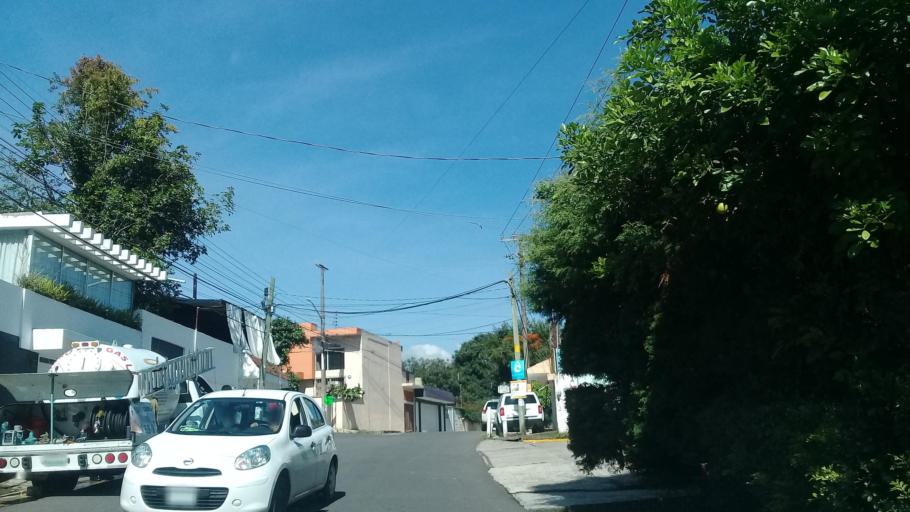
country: MX
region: Veracruz
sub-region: Xalapa
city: Xalapa de Enriquez
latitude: 19.5283
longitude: -96.9433
